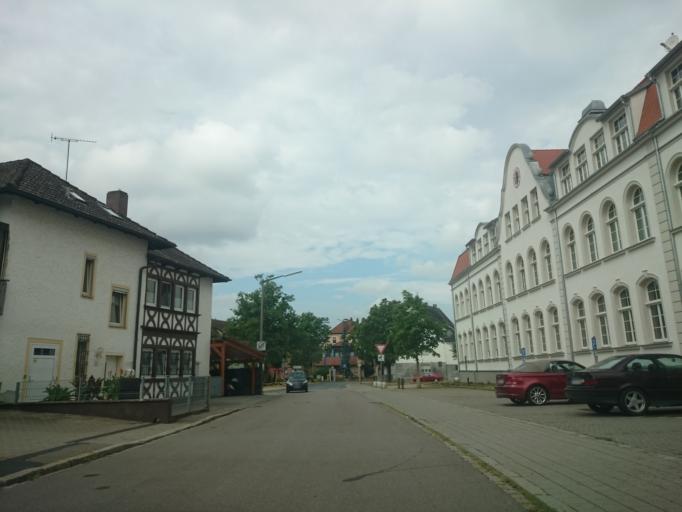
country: DE
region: Bavaria
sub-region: Regierungsbezirk Mittelfranken
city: Roth
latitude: 49.2444
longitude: 11.0986
